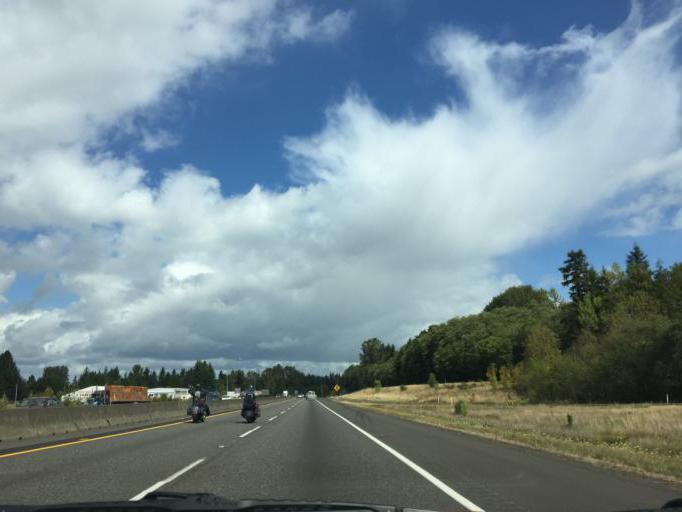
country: US
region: Washington
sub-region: Lewis County
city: Winlock
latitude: 46.3919
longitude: -122.9015
